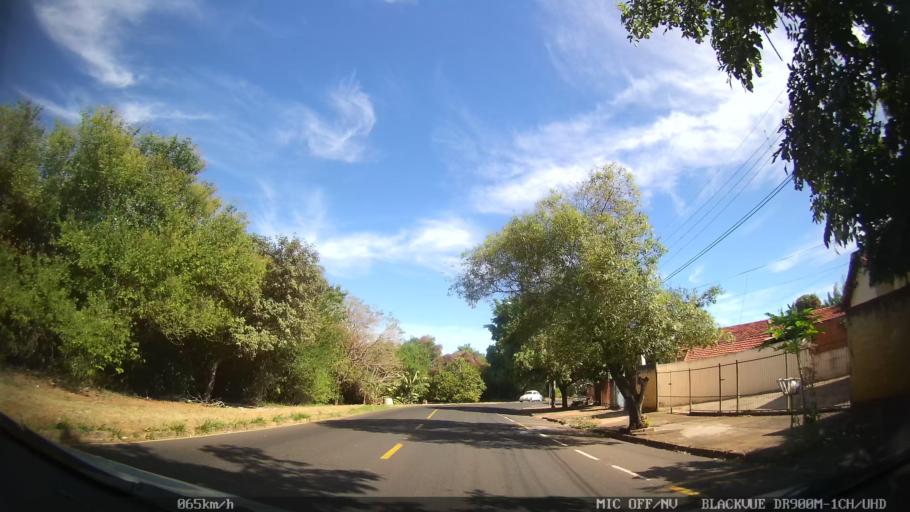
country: BR
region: Sao Paulo
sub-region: Sao Jose Do Rio Preto
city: Sao Jose do Rio Preto
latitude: -20.8502
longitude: -49.3645
